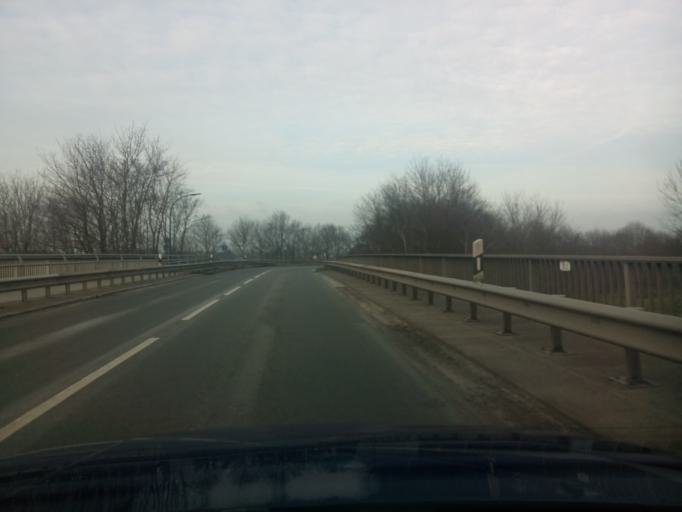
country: DE
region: Lower Saxony
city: Oyten
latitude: 53.0827
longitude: 9.0159
